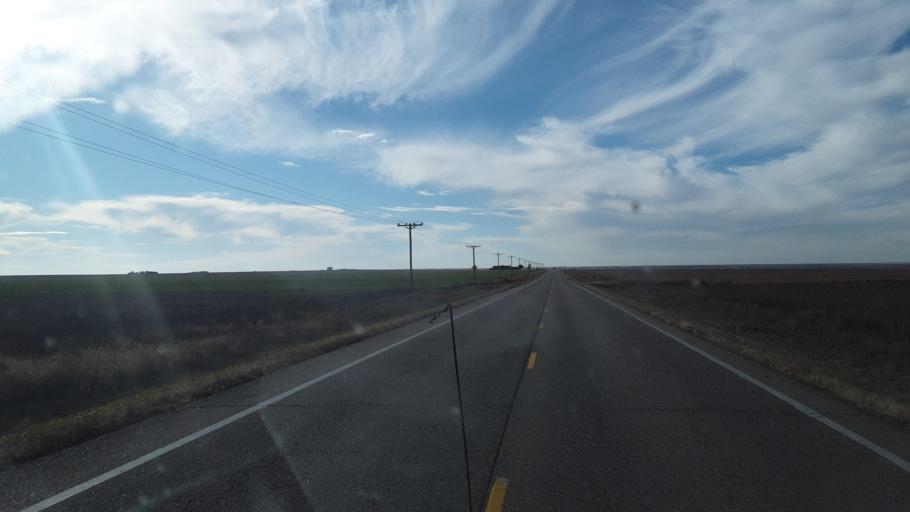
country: US
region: Kansas
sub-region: Gray County
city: Cimarron
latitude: 38.0591
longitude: -100.4891
